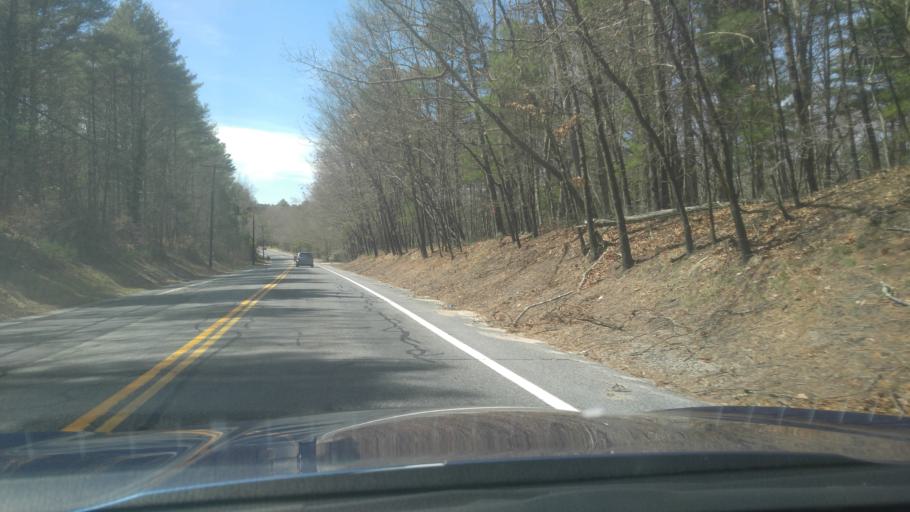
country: US
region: Rhode Island
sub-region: Kent County
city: West Greenwich
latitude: 41.5882
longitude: -71.6223
